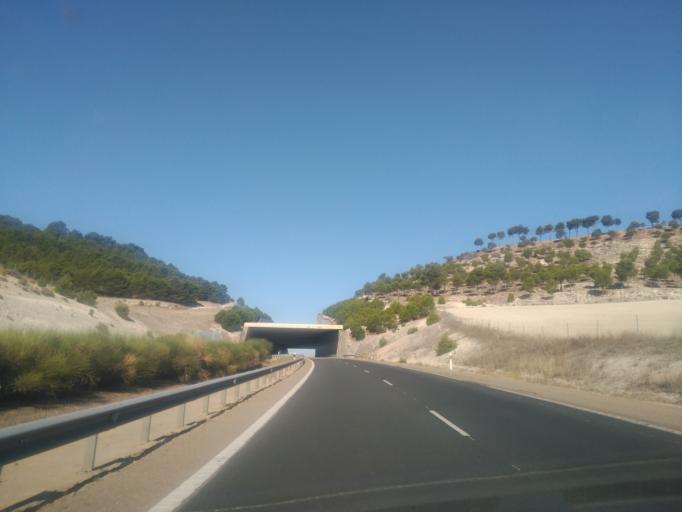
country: ES
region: Castille and Leon
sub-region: Provincia de Valladolid
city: Cisterniga
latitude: 41.6077
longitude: -4.6660
